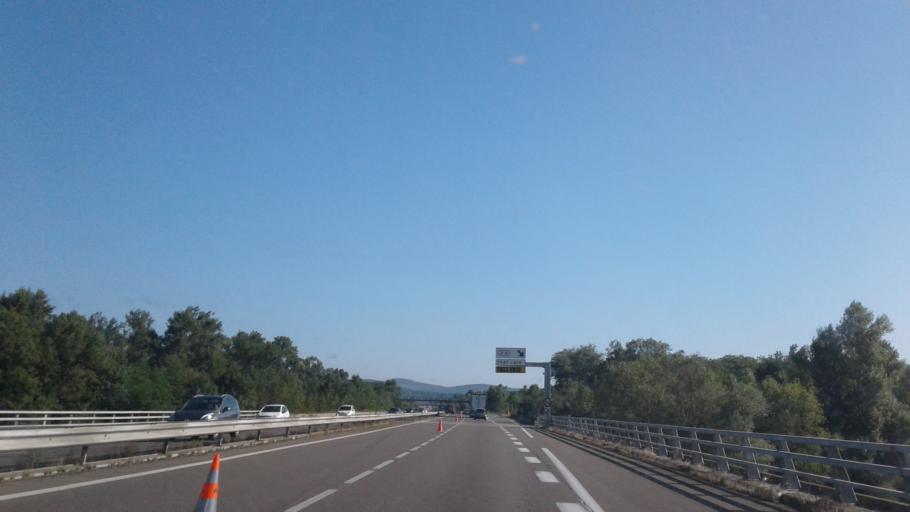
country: FR
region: Rhone-Alpes
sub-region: Departement de l'Ain
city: Ambronay
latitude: 46.0418
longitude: 5.3237
